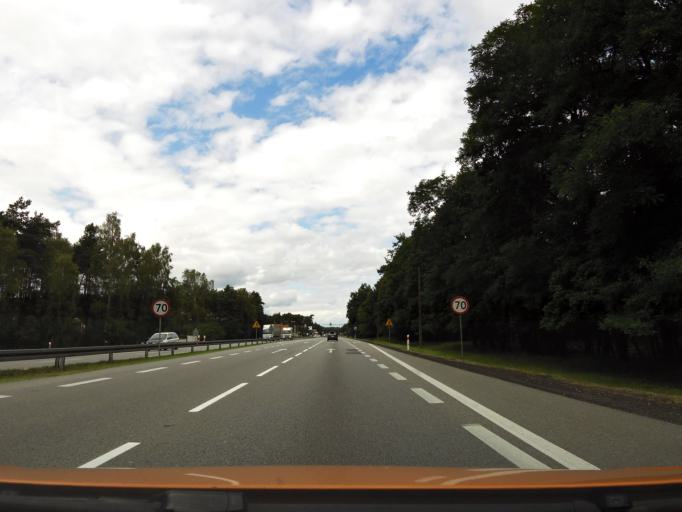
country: PL
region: West Pomeranian Voivodeship
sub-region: Powiat goleniowski
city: Goleniow
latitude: 53.4593
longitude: 14.7881
